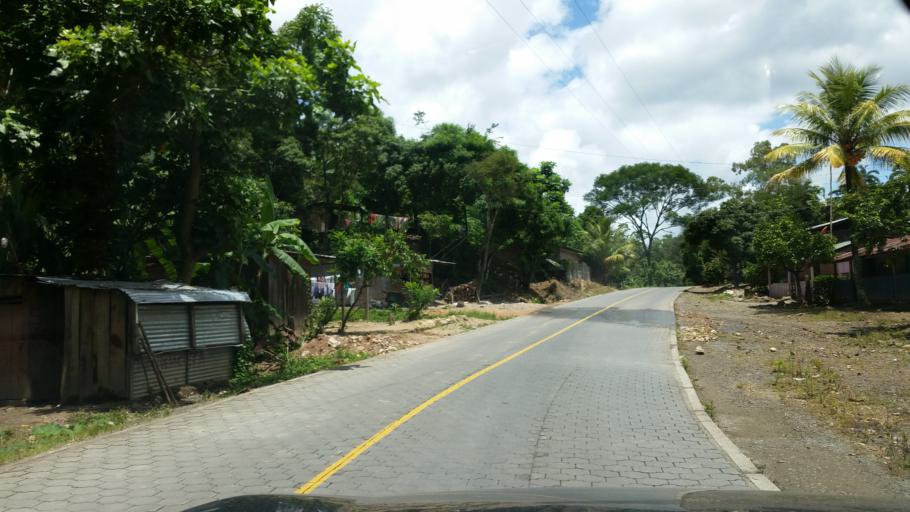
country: NI
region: Atlantico Norte (RAAN)
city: Waslala
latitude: 13.2484
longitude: -85.6141
